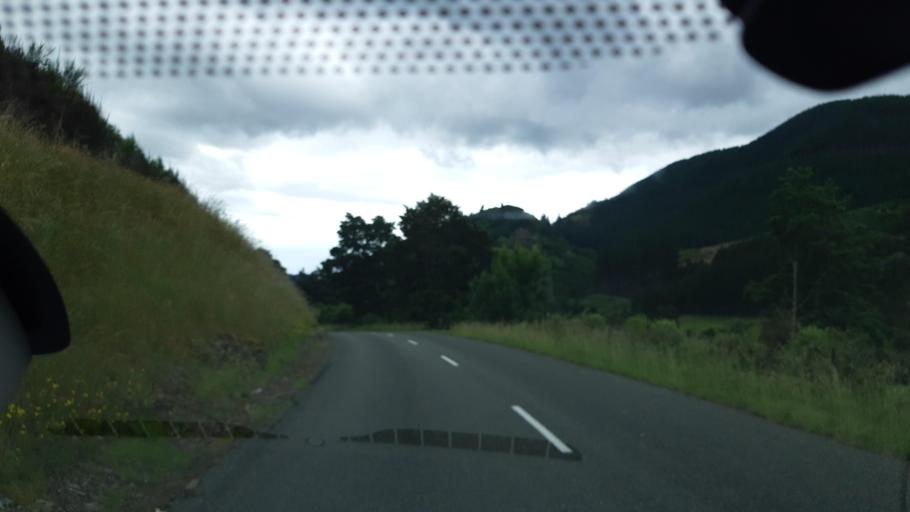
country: NZ
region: Tasman
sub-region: Tasman District
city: Brightwater
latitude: -41.4259
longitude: 173.1193
